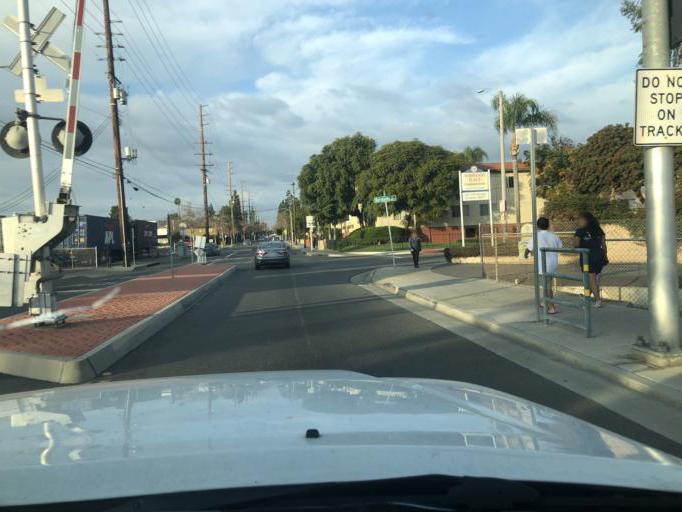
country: US
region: California
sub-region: Orange County
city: Tustin
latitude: 33.7352
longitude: -117.8449
